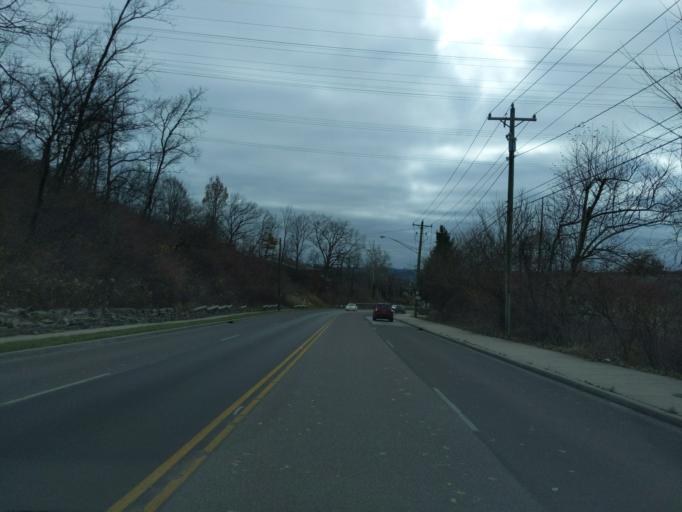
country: US
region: Ohio
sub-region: Hamilton County
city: Finneytown
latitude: 39.1816
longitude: -84.5445
